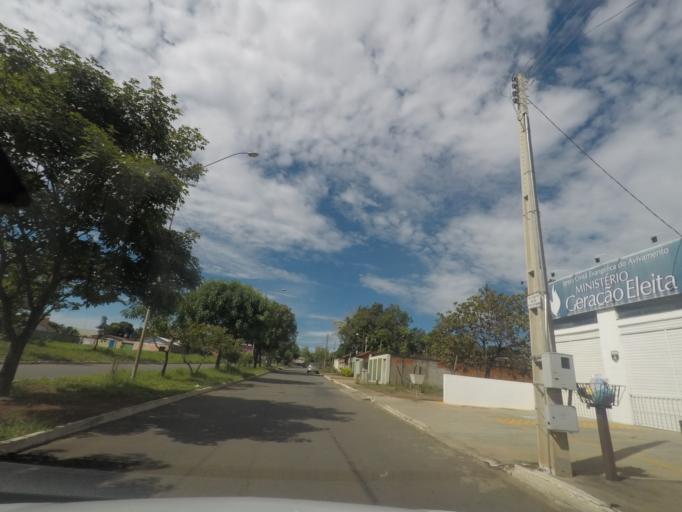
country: BR
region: Goias
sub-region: Aparecida De Goiania
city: Aparecida de Goiania
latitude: -16.8186
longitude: -49.2908
